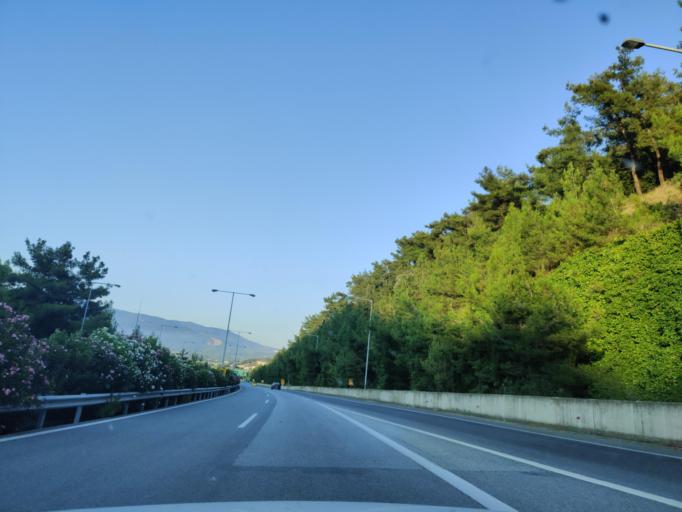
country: GR
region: East Macedonia and Thrace
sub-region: Nomos Kavalas
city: Kavala
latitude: 40.9530
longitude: 24.4570
